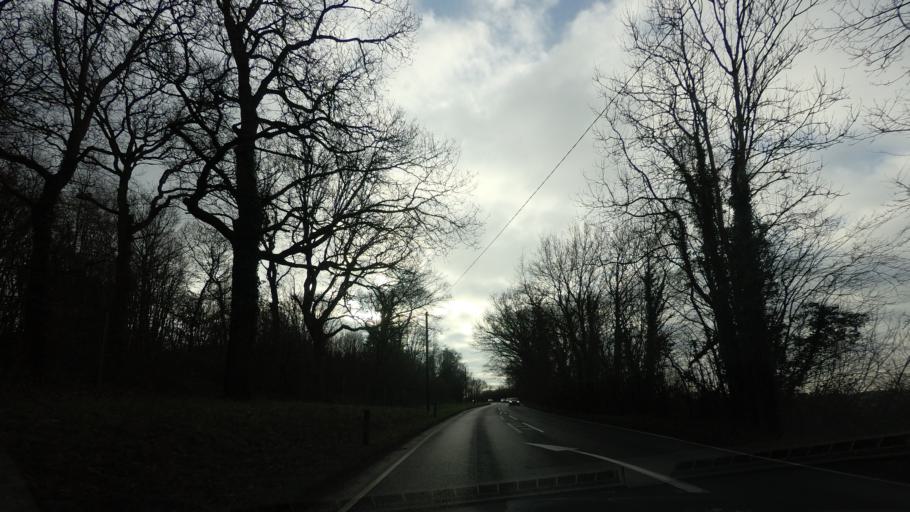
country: GB
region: England
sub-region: Kent
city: Hawkhurst
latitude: 51.0472
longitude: 0.4474
